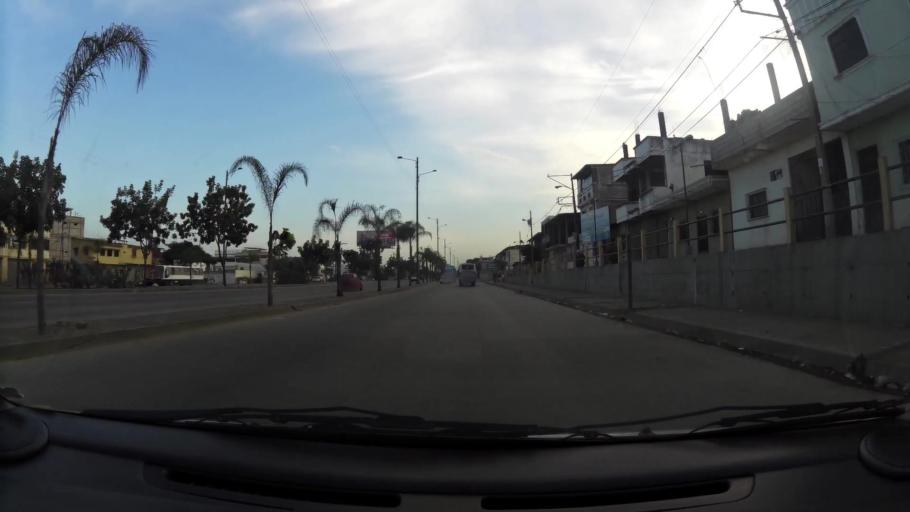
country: EC
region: Guayas
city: Eloy Alfaro
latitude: -2.1251
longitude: -79.8824
